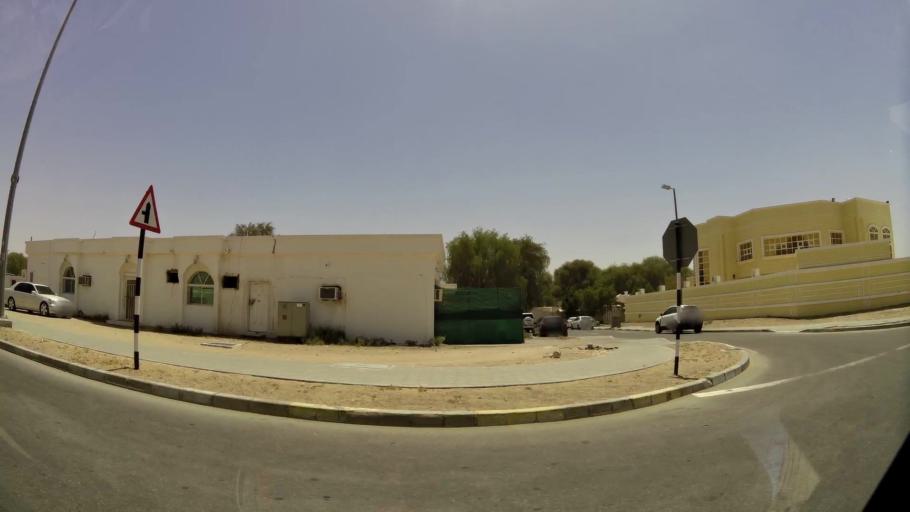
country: OM
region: Al Buraimi
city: Al Buraymi
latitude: 24.2736
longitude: 55.7457
